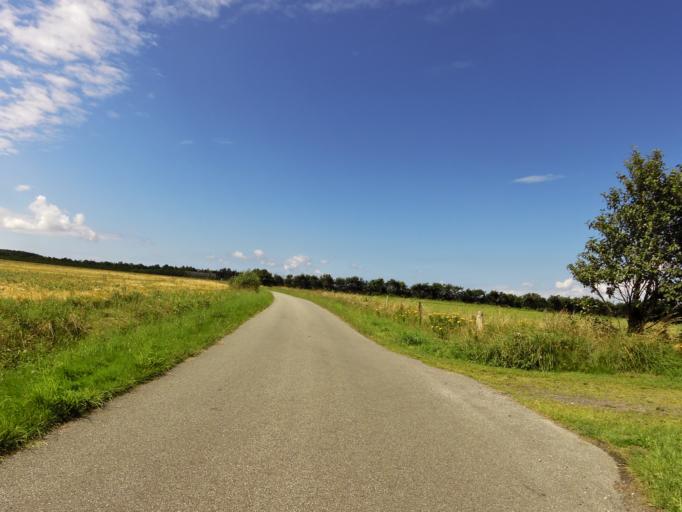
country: DK
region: South Denmark
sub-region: Esbjerg Kommune
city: Ribe
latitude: 55.3082
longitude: 8.7907
